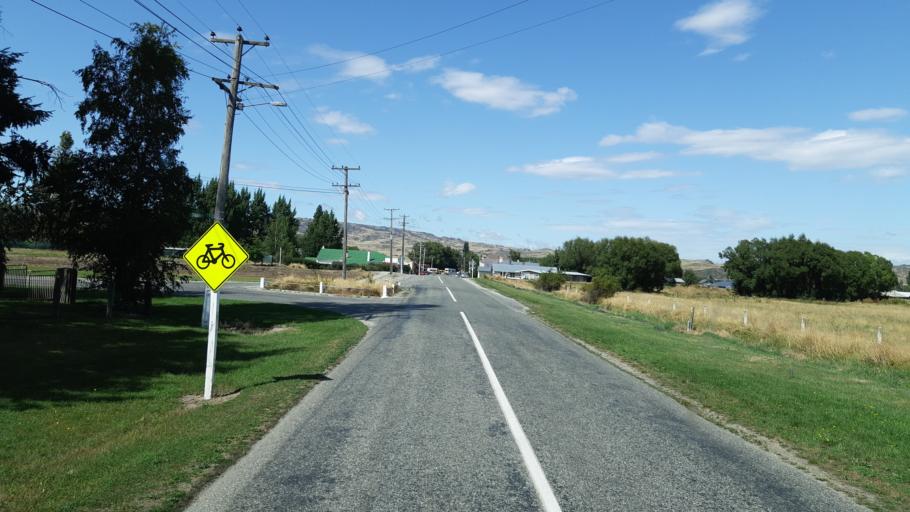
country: NZ
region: Otago
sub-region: Queenstown-Lakes District
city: Wanaka
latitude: -45.0913
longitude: 169.6019
